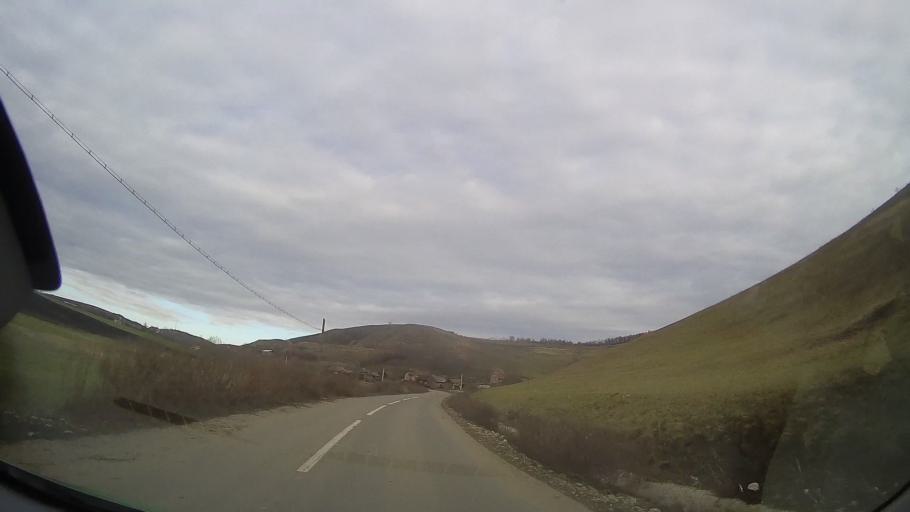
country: RO
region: Bistrita-Nasaud
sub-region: Comuna Micestii de Campie
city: Micestii de Campie
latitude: 46.8285
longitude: 24.3060
